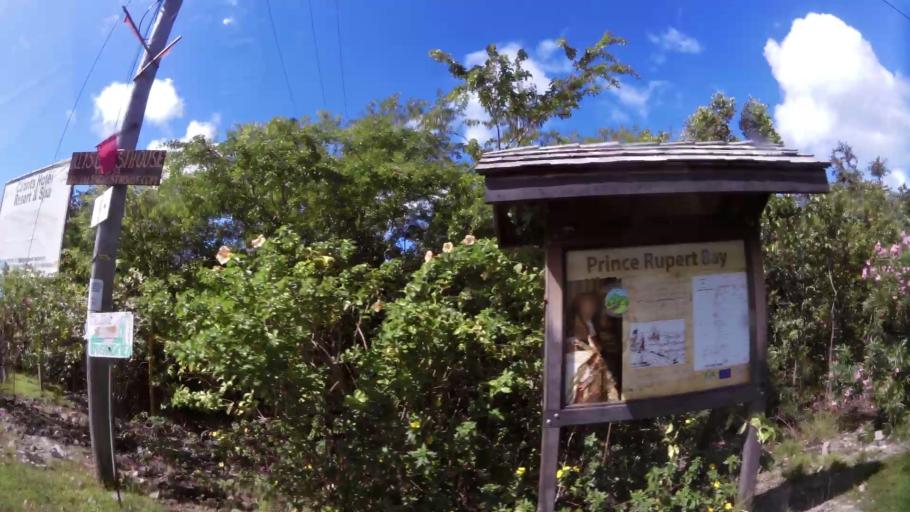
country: DM
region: Saint John
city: Portsmouth
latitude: 15.5850
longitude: -61.4642
